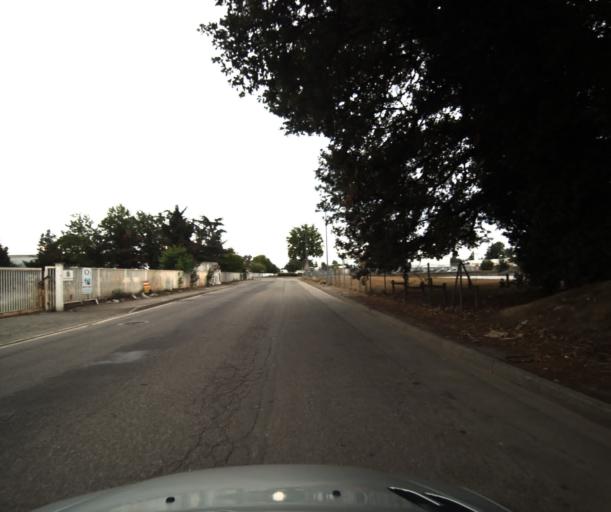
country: FR
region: Midi-Pyrenees
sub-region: Departement de la Haute-Garonne
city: Pinsaguel
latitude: 43.5287
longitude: 1.3813
